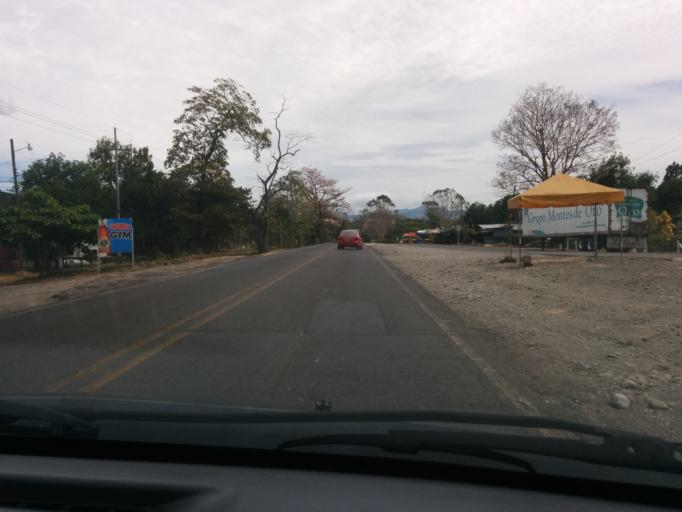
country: CR
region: Puntarenas
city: Esparza
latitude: 10.0007
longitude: -84.6455
